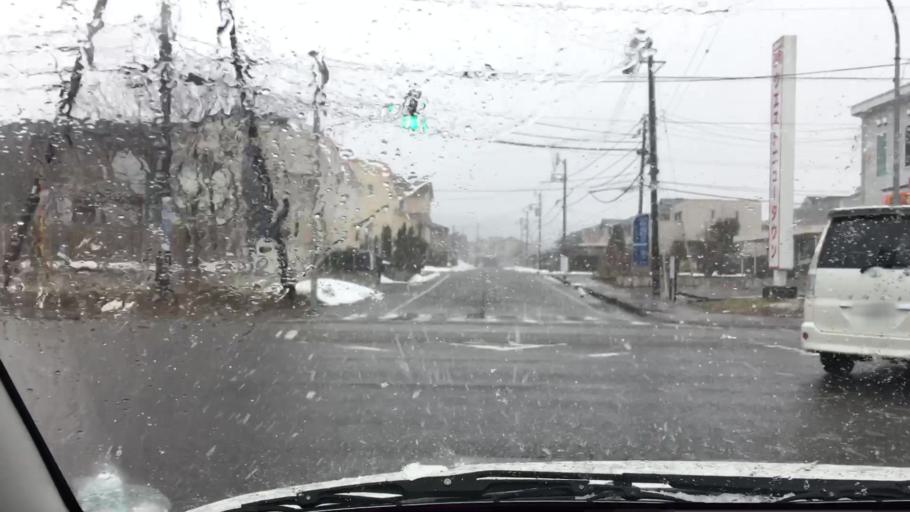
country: JP
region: Niigata
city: Joetsu
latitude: 37.1144
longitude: 138.2332
